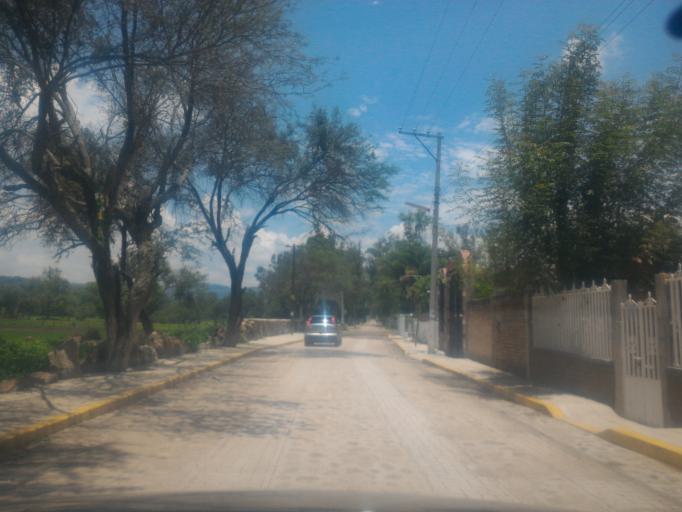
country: MX
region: Guanajuato
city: Ciudad Manuel Doblado
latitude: 20.7963
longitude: -101.9962
